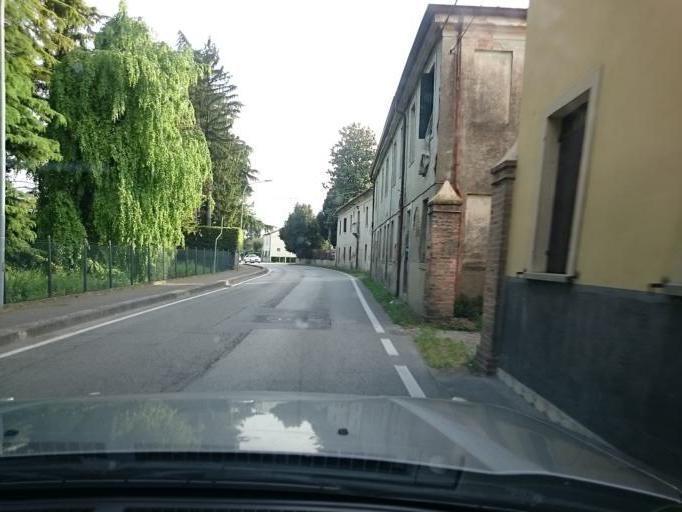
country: IT
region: Veneto
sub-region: Provincia di Padova
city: Noventa
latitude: 45.4059
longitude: 11.9457
